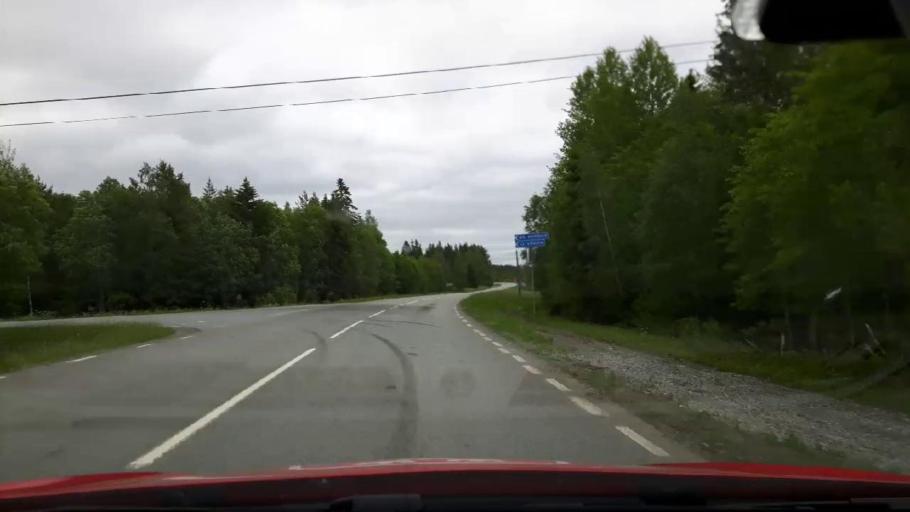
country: SE
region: Jaemtland
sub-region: Stroemsunds Kommun
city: Stroemsund
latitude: 63.5355
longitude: 15.4465
